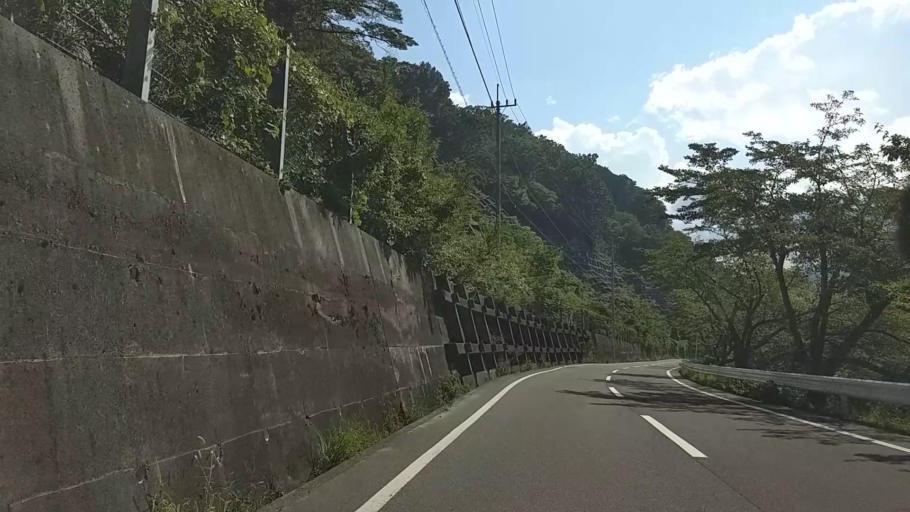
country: JP
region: Yamanashi
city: Fujikawaguchiko
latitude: 35.4051
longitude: 138.4551
